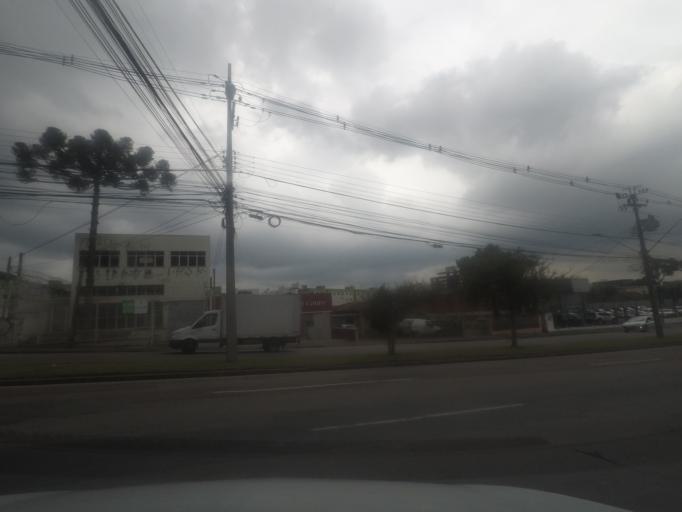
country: BR
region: Parana
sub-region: Curitiba
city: Curitiba
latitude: -25.4505
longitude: -49.3048
